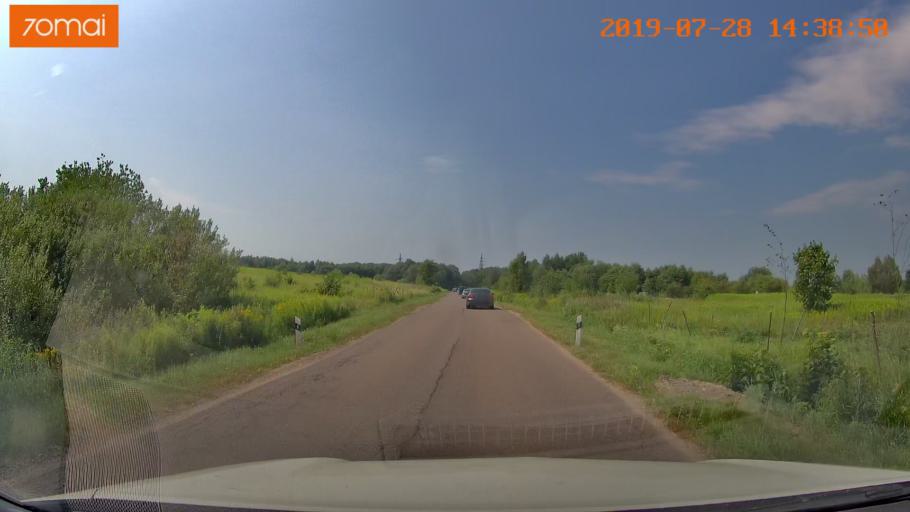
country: RU
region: Kaliningrad
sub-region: Gorod Kaliningrad
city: Yantarnyy
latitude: 54.8460
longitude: 19.9785
